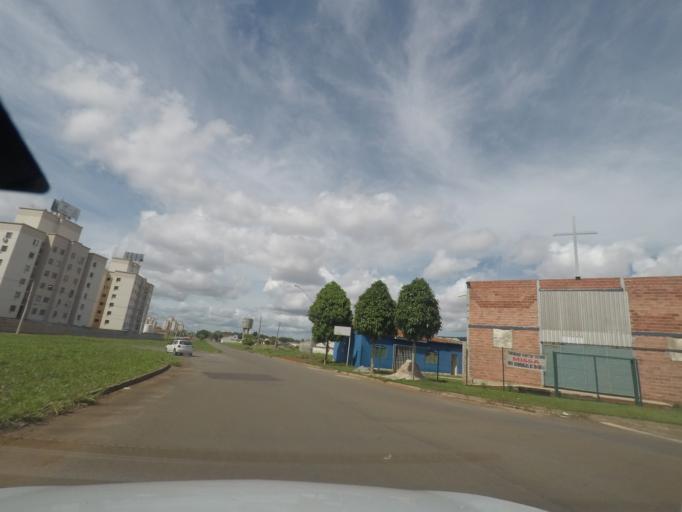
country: BR
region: Goias
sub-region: Goiania
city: Goiania
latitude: -16.7209
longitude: -49.3491
